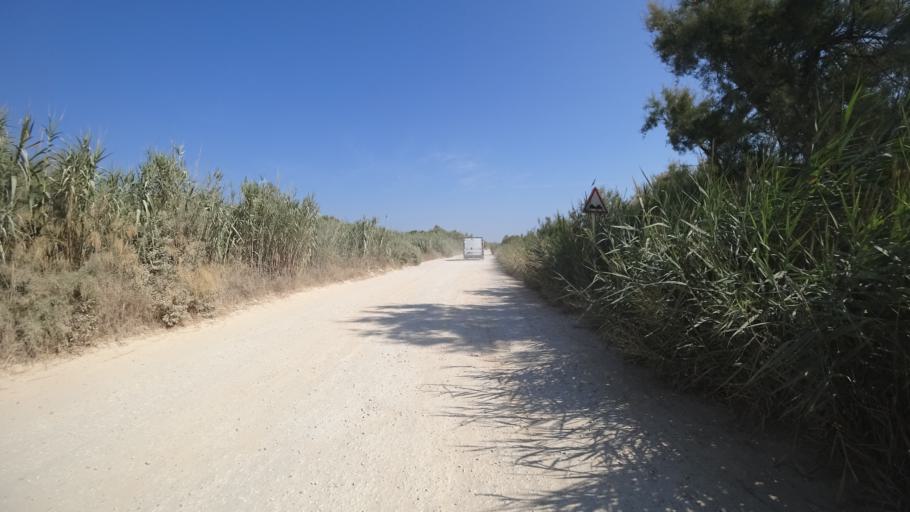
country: FR
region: Languedoc-Roussillon
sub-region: Departement des Pyrenees-Orientales
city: Le Barcares
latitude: 42.7700
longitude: 3.0355
